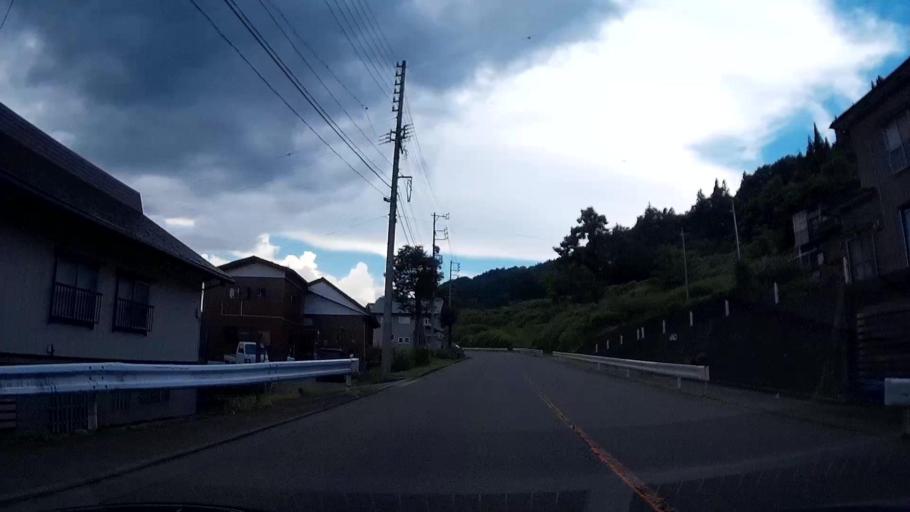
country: JP
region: Nagano
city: Iiyama
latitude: 36.9855
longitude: 138.5268
